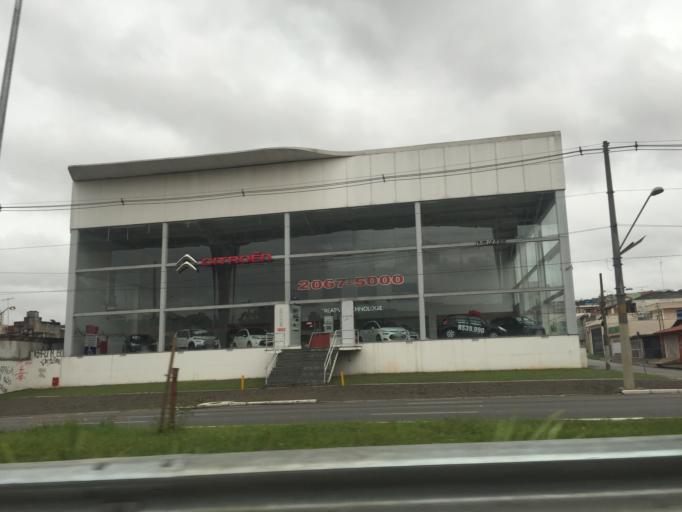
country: BR
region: Sao Paulo
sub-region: Sao Caetano Do Sul
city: Sao Caetano do Sul
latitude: -23.5837
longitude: -46.5754
